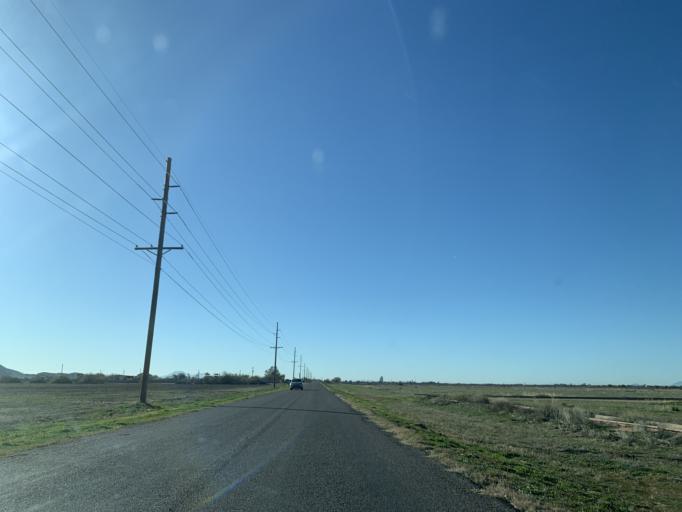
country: US
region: Arizona
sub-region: Pinal County
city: Casa Grande
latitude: 32.8505
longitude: -111.6746
